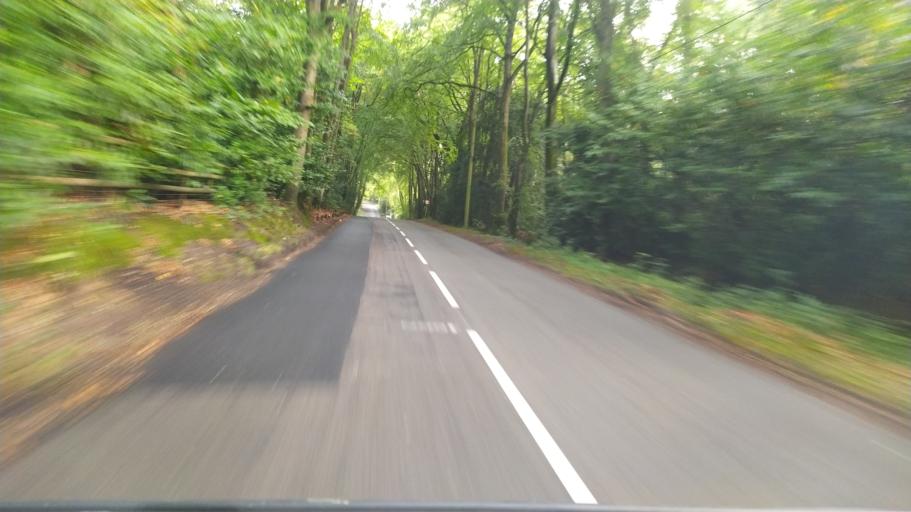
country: GB
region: England
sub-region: Hampshire
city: West Wellow
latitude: 51.0071
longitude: -1.5479
